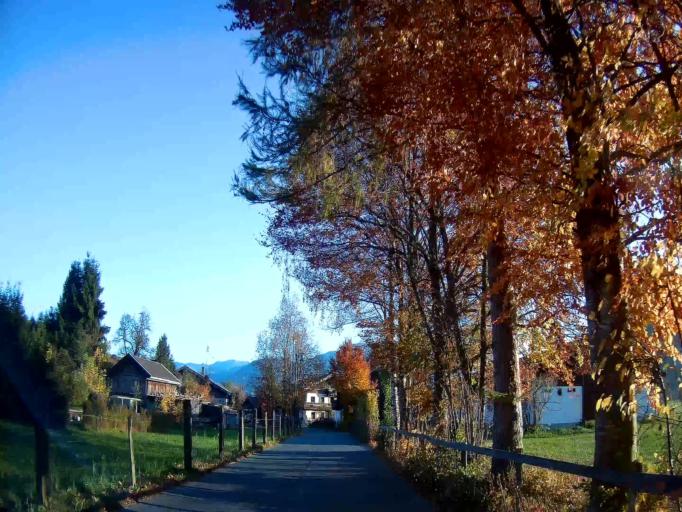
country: AT
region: Salzburg
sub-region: Politischer Bezirk Zell am See
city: Saalfelden am Steinernen Meer
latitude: 47.4464
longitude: 12.8161
